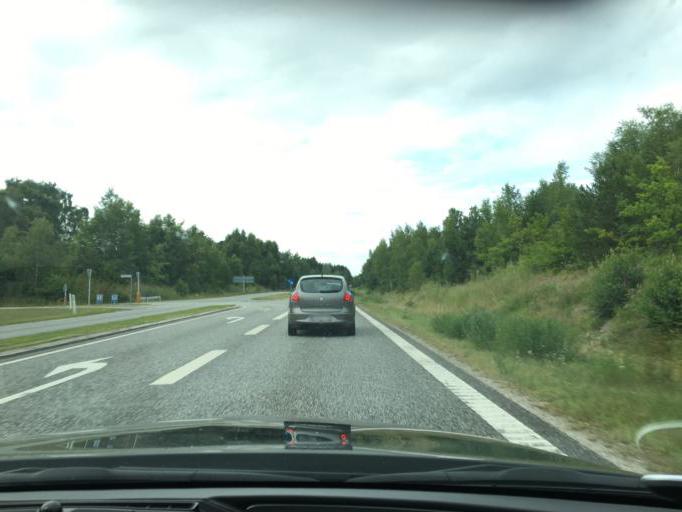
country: DK
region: Capital Region
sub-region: Gribskov Kommune
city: Helsinge
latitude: 55.9962
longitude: 12.2423
